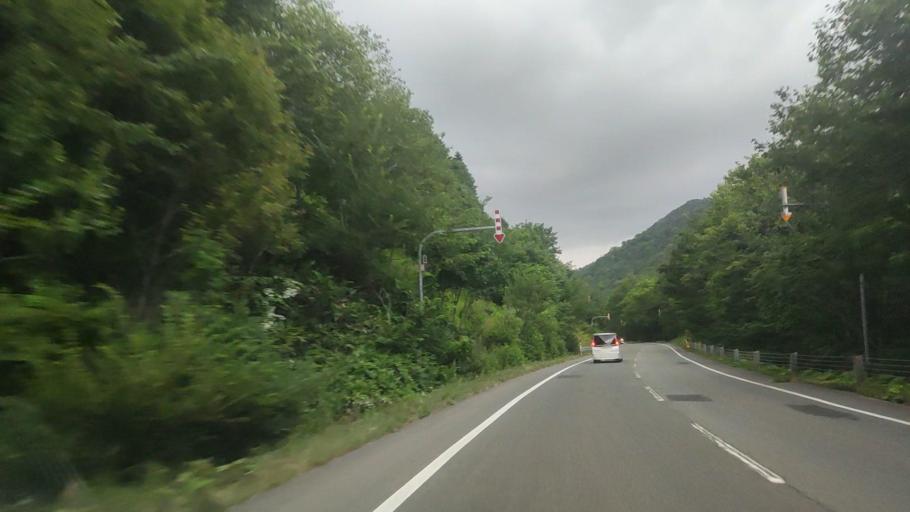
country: JP
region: Hokkaido
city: Shimo-furano
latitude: 43.3612
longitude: 142.3110
